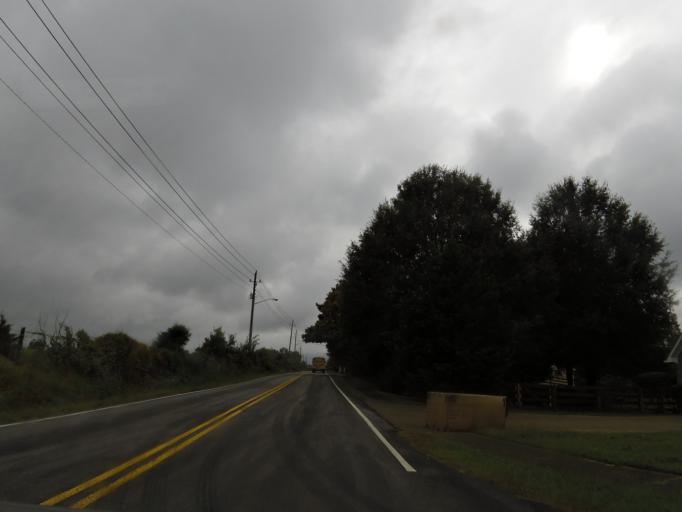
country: US
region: Tennessee
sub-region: Bradley County
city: Hopewell
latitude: 35.2048
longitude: -84.9045
